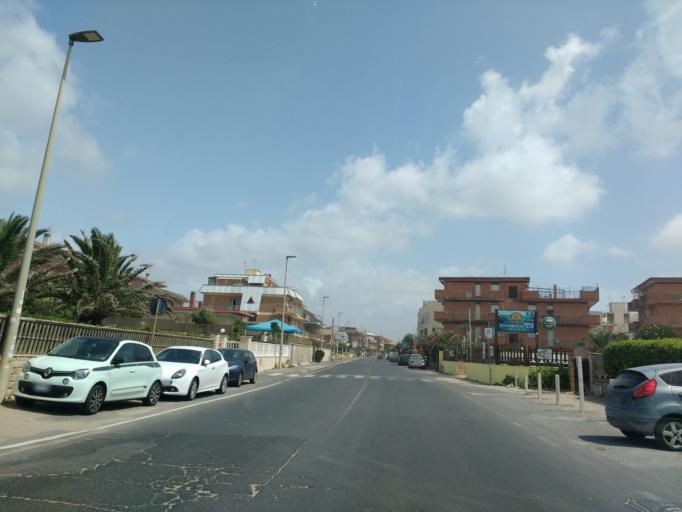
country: IT
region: Latium
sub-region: Citta metropolitana di Roma Capitale
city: Torvaianica
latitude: 41.6331
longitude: 12.4477
